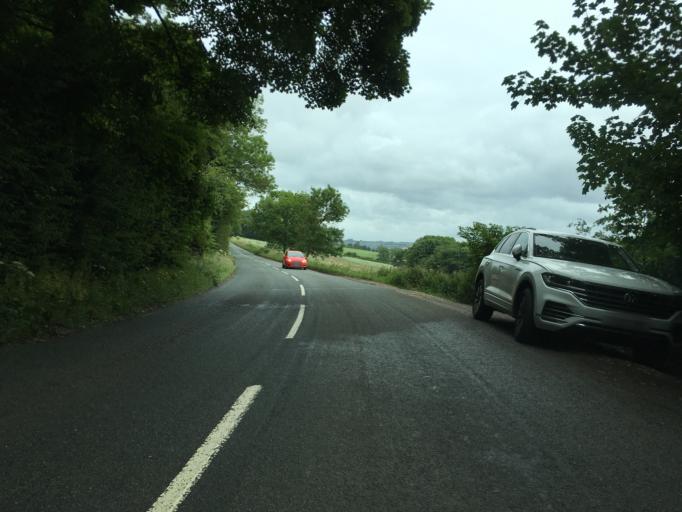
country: GB
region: England
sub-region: Gloucestershire
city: Chipping Campden
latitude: 52.0480
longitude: -1.8057
